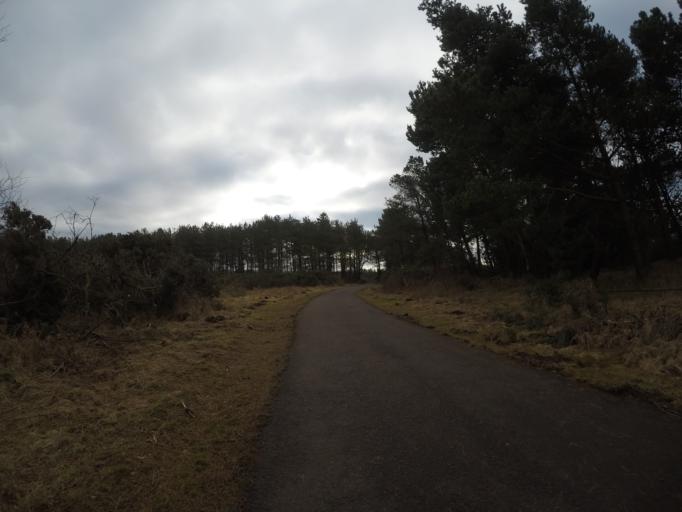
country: GB
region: Scotland
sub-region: North Ayrshire
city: Irvine
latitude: 55.5947
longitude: -4.6728
